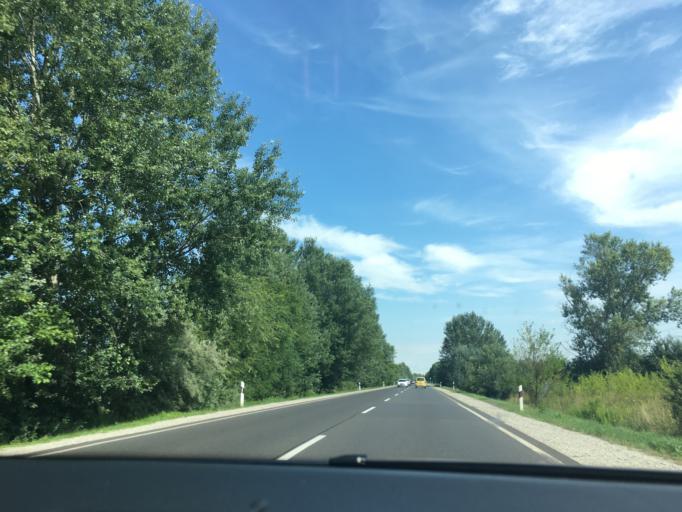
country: HU
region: Szabolcs-Szatmar-Bereg
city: Ujfeherto
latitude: 47.8418
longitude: 21.7046
